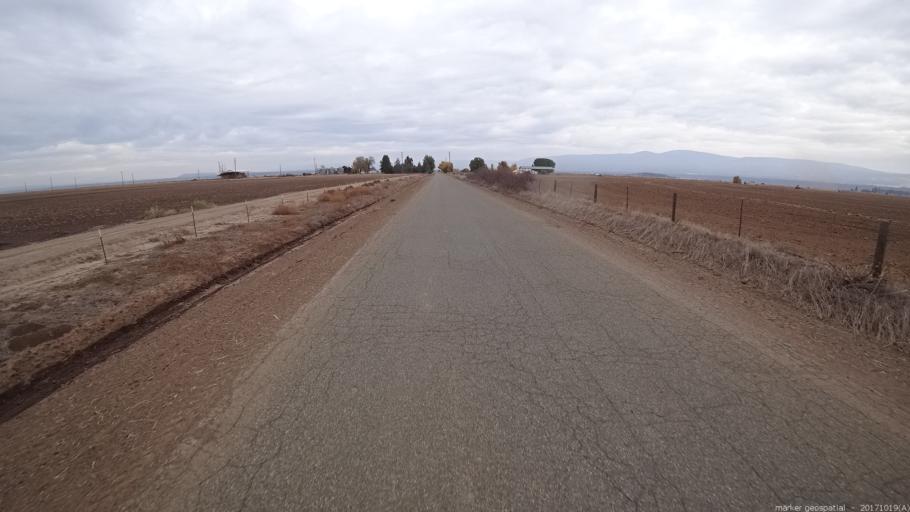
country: US
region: California
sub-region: Shasta County
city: Burney
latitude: 41.0626
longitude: -121.3891
